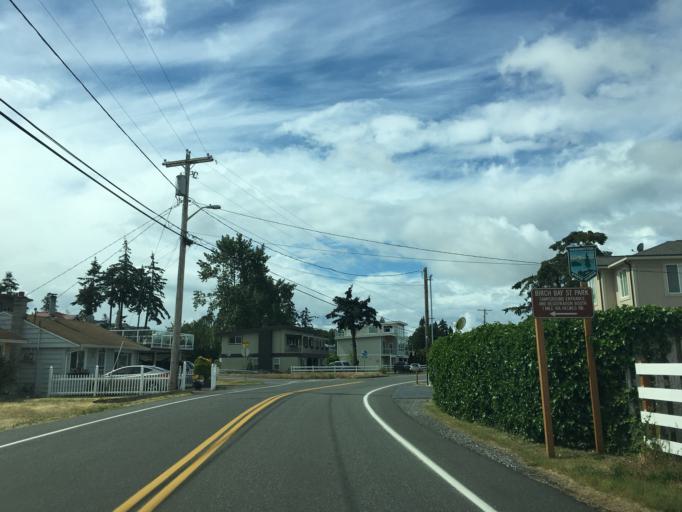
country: US
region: Washington
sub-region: Whatcom County
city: Birch Bay
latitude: 48.9134
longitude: -122.7481
